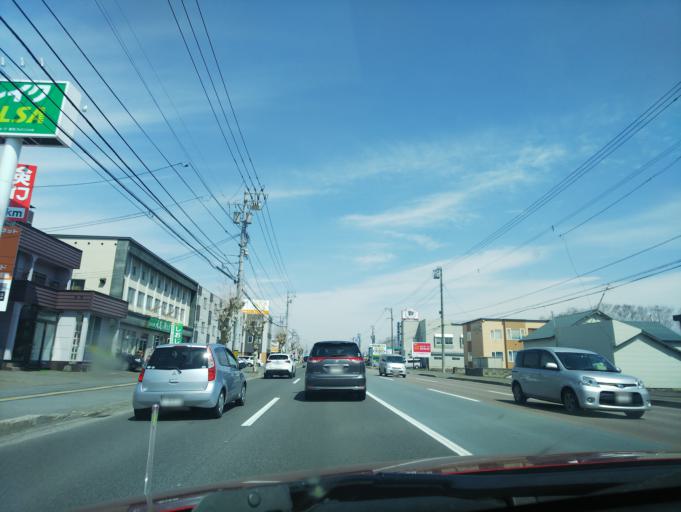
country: JP
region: Hokkaido
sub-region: Asahikawa-shi
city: Asahikawa
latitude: 43.7823
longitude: 142.3888
